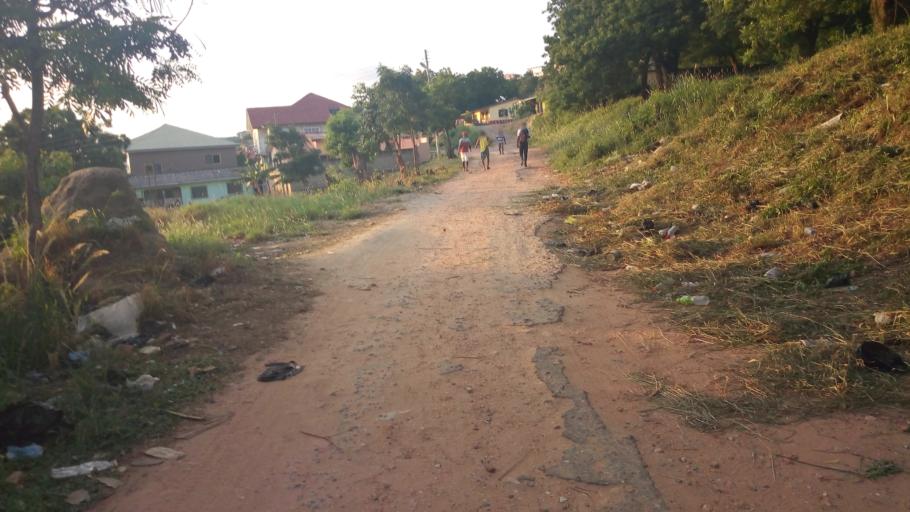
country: GH
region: Greater Accra
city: Gbawe
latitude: 5.5584
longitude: -0.3040
